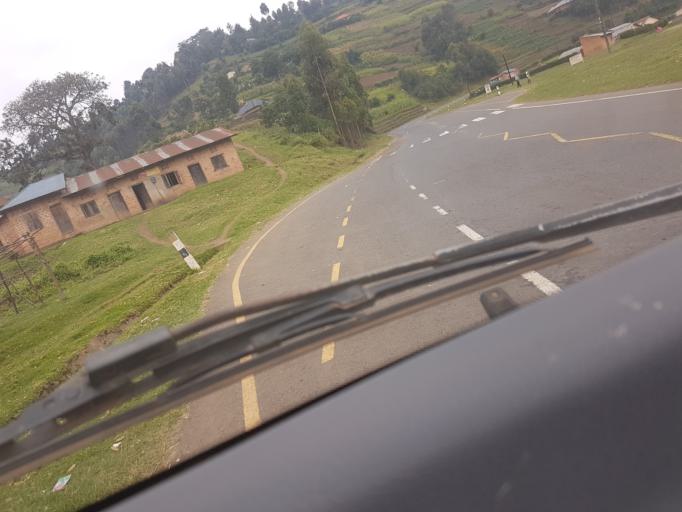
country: UG
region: Western Region
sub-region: Kisoro District
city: Kisoro
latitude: -1.2043
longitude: 29.8112
